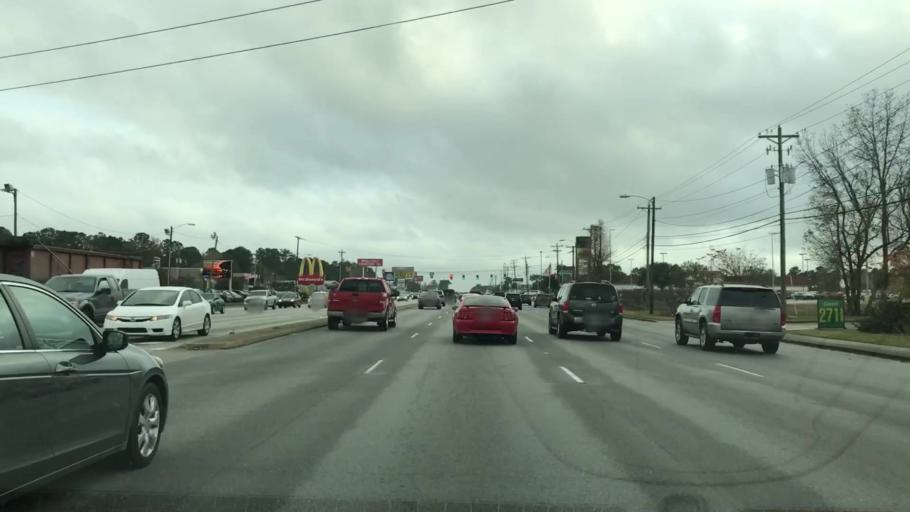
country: US
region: South Carolina
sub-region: Berkeley County
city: Goose Creek
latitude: 32.9650
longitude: -80.0443
